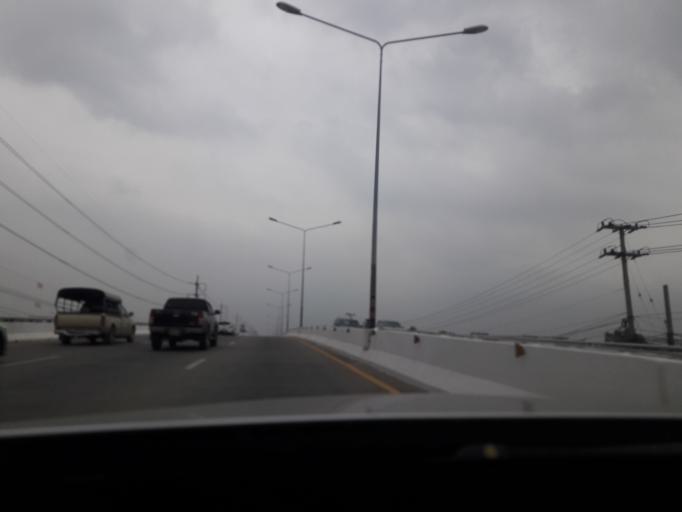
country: TH
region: Samut Songkhram
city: Samut Songkhram
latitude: 13.4159
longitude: 99.9974
